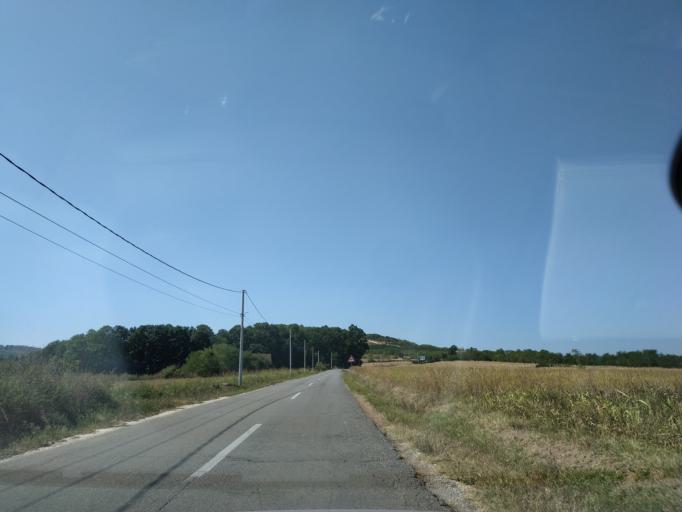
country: RS
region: Central Serbia
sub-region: Sumadijski Okrug
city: Topola
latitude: 44.2681
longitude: 20.6583
